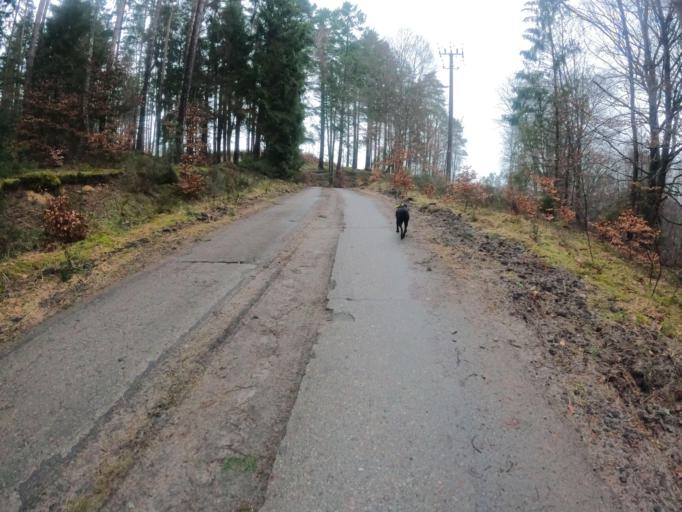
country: PL
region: West Pomeranian Voivodeship
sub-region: Powiat koszalinski
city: Polanow
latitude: 54.2257
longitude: 16.7220
